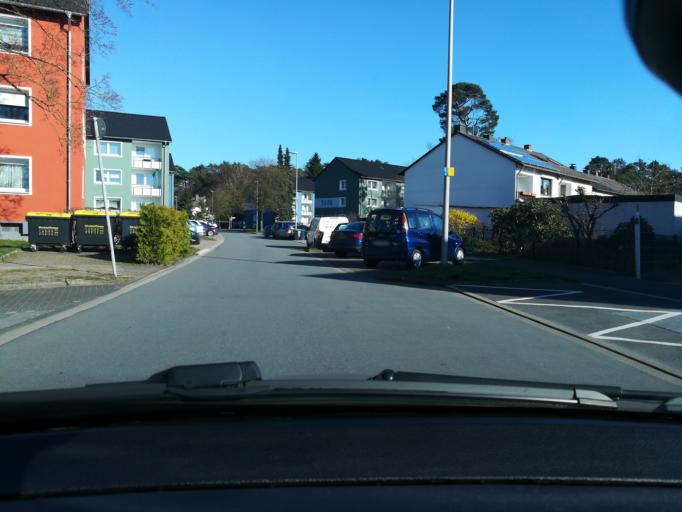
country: DE
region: North Rhine-Westphalia
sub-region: Regierungsbezirk Detmold
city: Oerlinghausen
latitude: 51.9514
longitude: 8.5984
